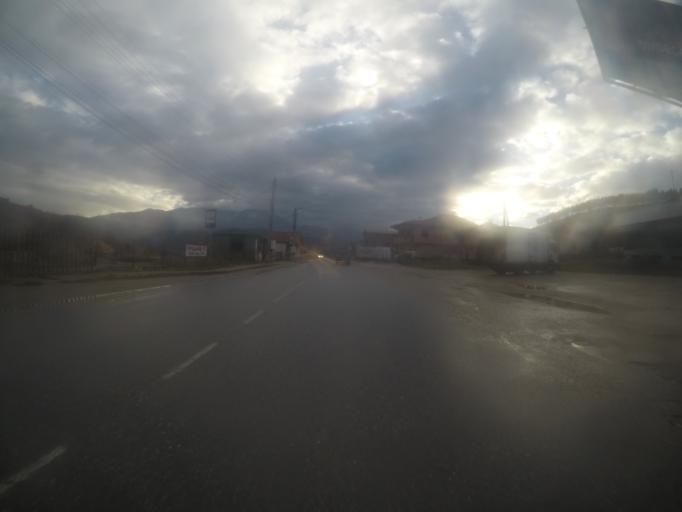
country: BG
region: Blagoevgrad
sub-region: Obshtina Simitli
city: Simitli
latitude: 41.8806
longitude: 23.1245
